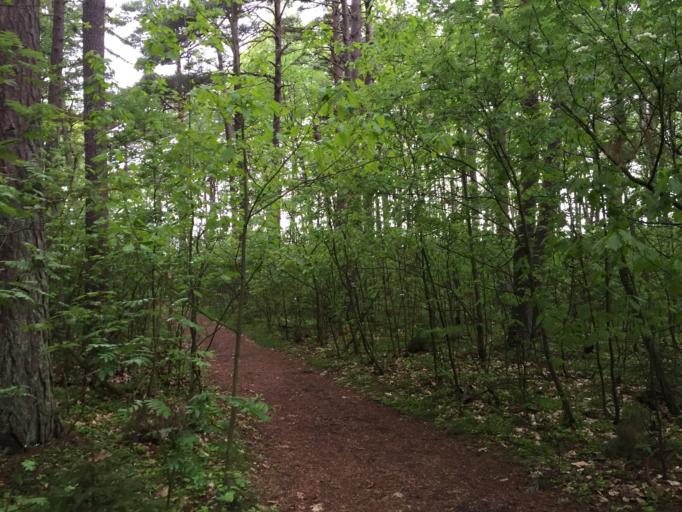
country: LT
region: Klaipedos apskritis
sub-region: Klaipeda
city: Klaipeda
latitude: 55.7957
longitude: 21.0694
